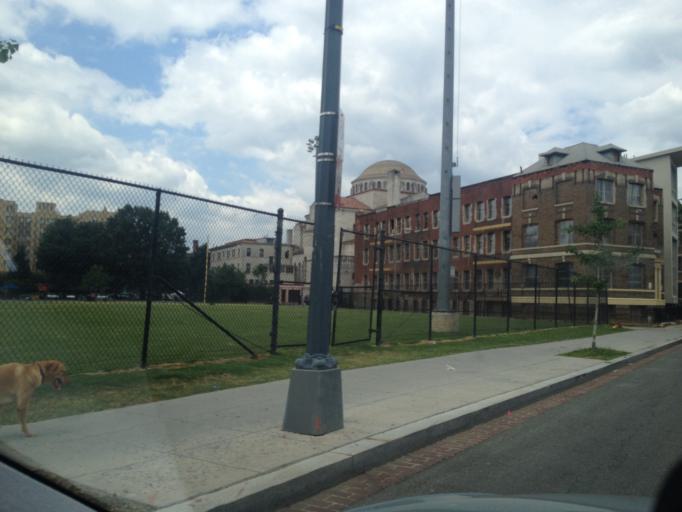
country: US
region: Washington, D.C.
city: Washington, D.C.
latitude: 38.9300
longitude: -77.0348
